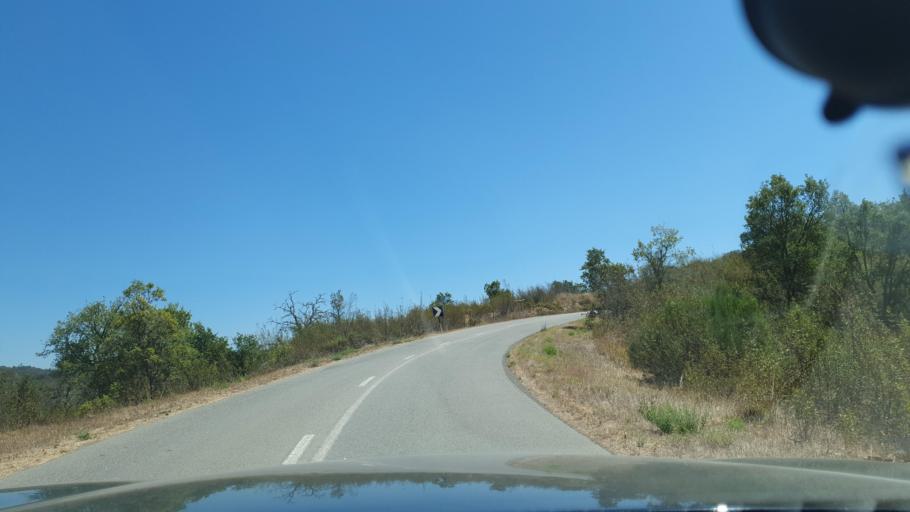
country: PT
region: Beja
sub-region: Odemira
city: Odemira
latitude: 37.5536
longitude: -8.4346
